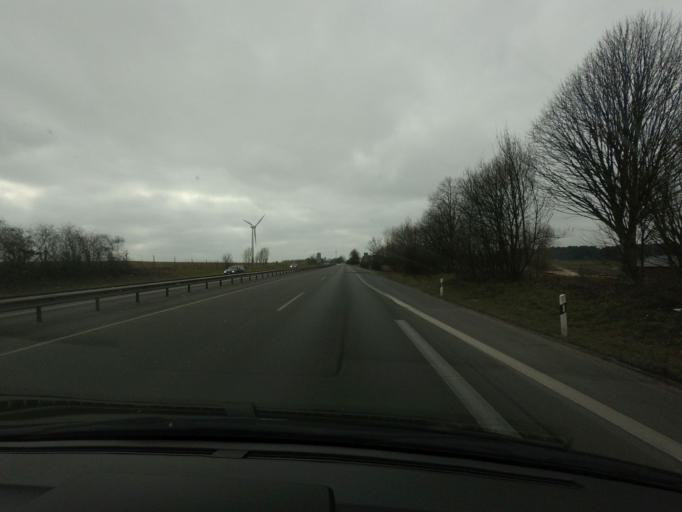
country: DE
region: Lower Saxony
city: Seevetal
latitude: 53.3991
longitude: 9.8980
